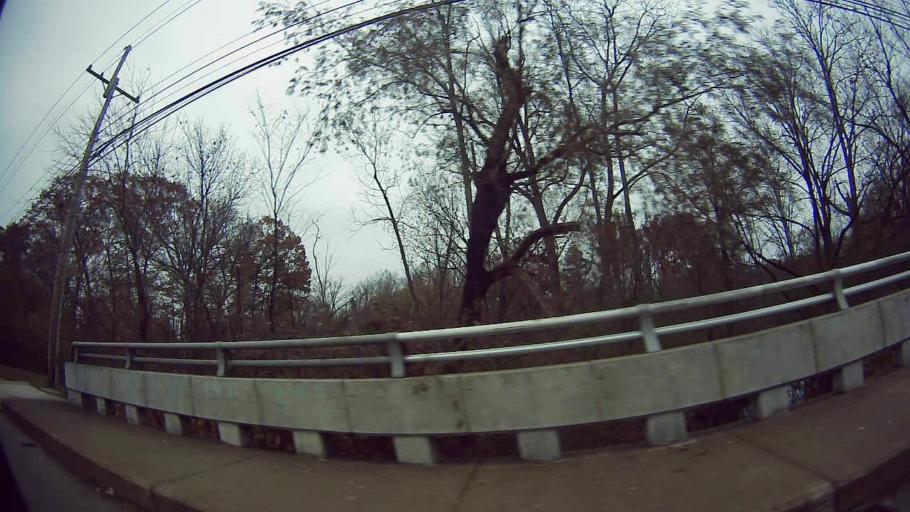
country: US
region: Michigan
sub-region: Oakland County
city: Southfield
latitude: 42.4676
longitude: -83.2605
